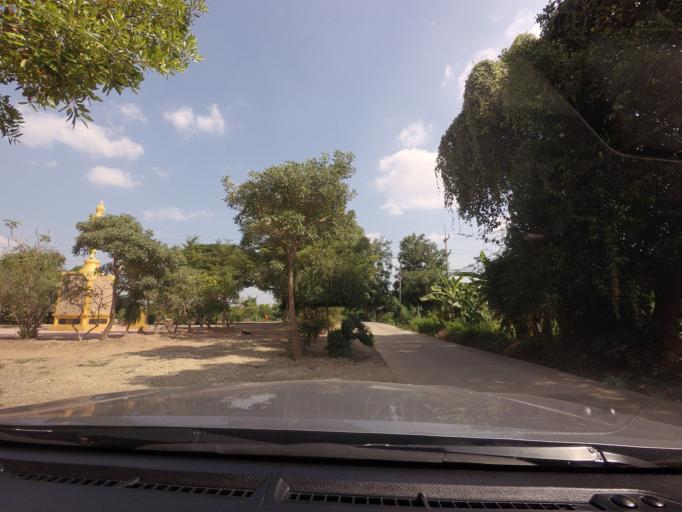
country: TH
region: Phitsanulok
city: Phitsanulok
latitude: 16.8194
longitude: 100.2347
